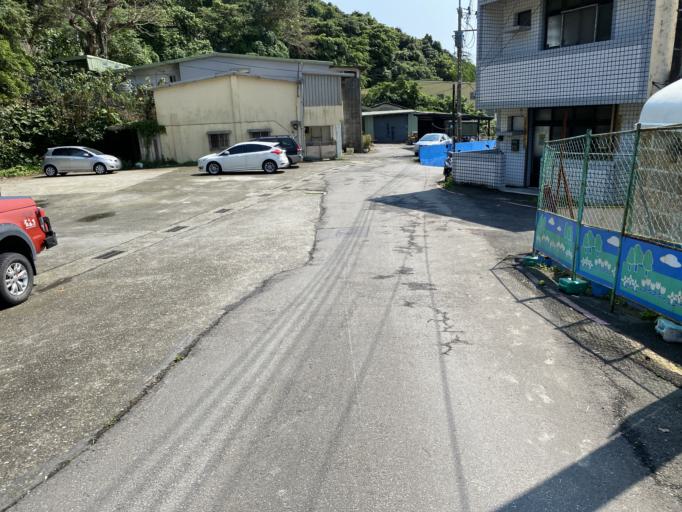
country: TW
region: Taiwan
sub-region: Keelung
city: Keelung
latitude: 25.1549
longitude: 121.7434
